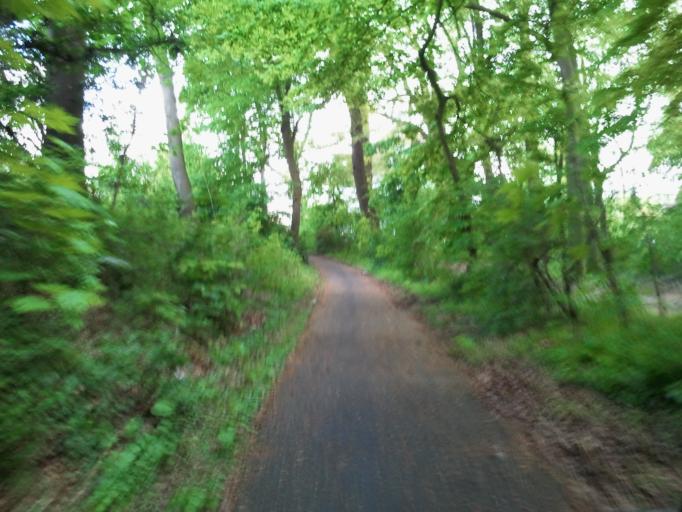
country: DE
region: Lower Saxony
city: Ritterhude
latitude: 53.1307
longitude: 8.7419
